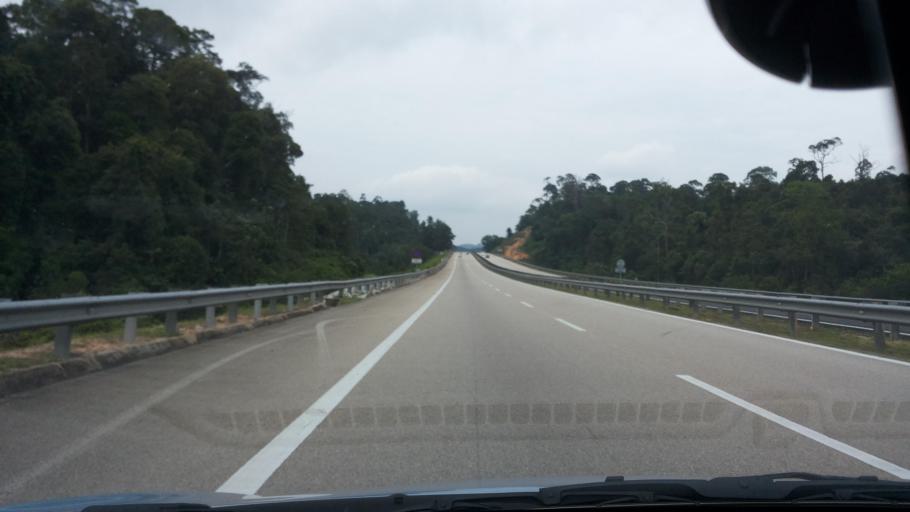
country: MY
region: Pahang
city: Kuantan
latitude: 3.7676
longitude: 103.1450
